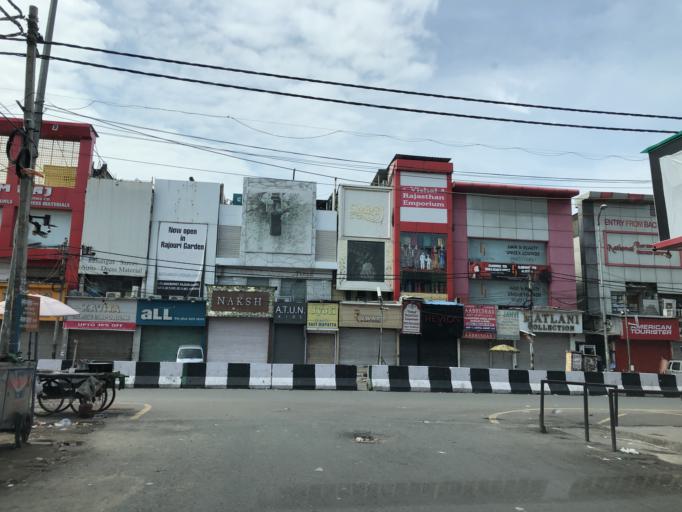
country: IN
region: NCT
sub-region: New Delhi
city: New Delhi
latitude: 28.5700
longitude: 77.2422
